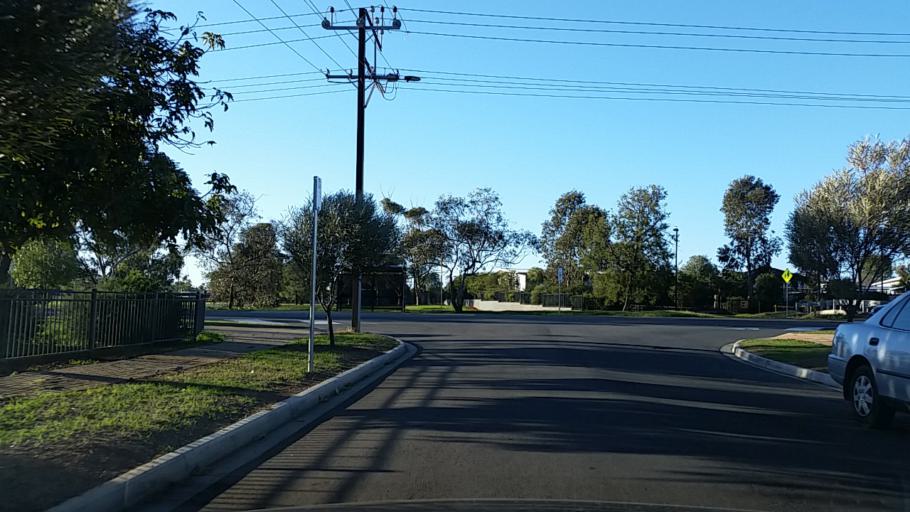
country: AU
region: South Australia
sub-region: Playford
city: Smithfield
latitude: -34.6805
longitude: 138.6709
